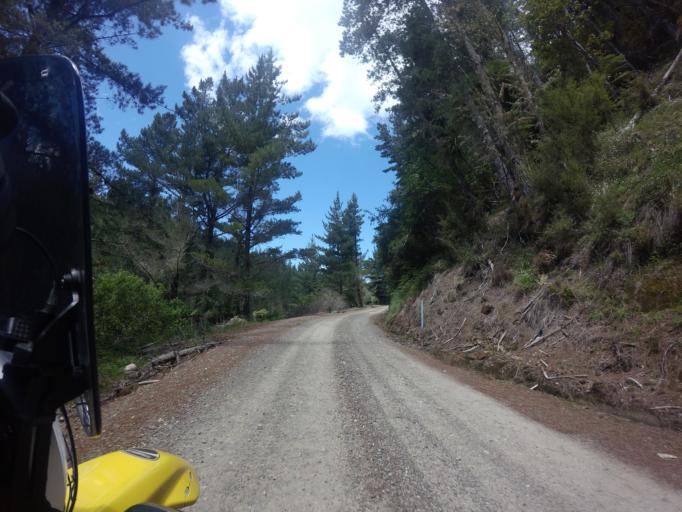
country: NZ
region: Hawke's Bay
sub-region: Wairoa District
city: Wairoa
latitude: -38.9733
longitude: 177.6877
